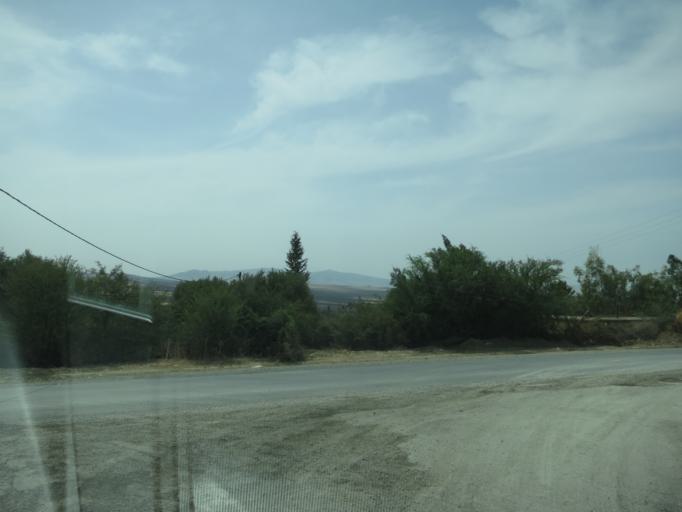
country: MA
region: Meknes-Tafilalet
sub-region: Meknes
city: Meknes
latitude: 34.0745
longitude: -5.5438
